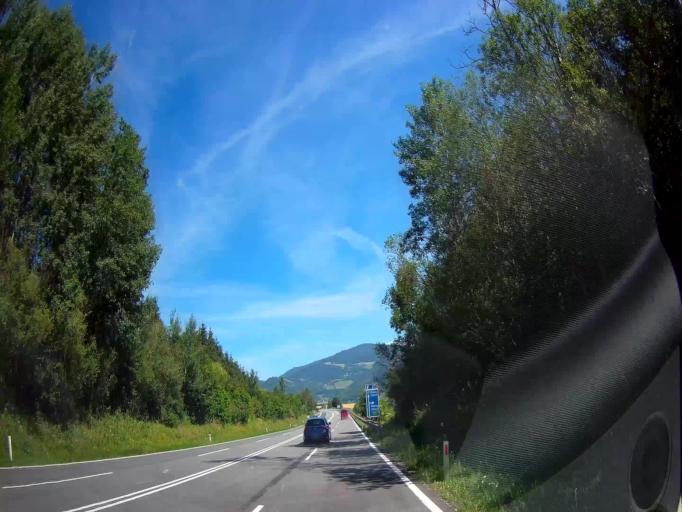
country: AT
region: Carinthia
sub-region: Politischer Bezirk Sankt Veit an der Glan
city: Molbling
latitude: 46.8578
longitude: 14.4491
